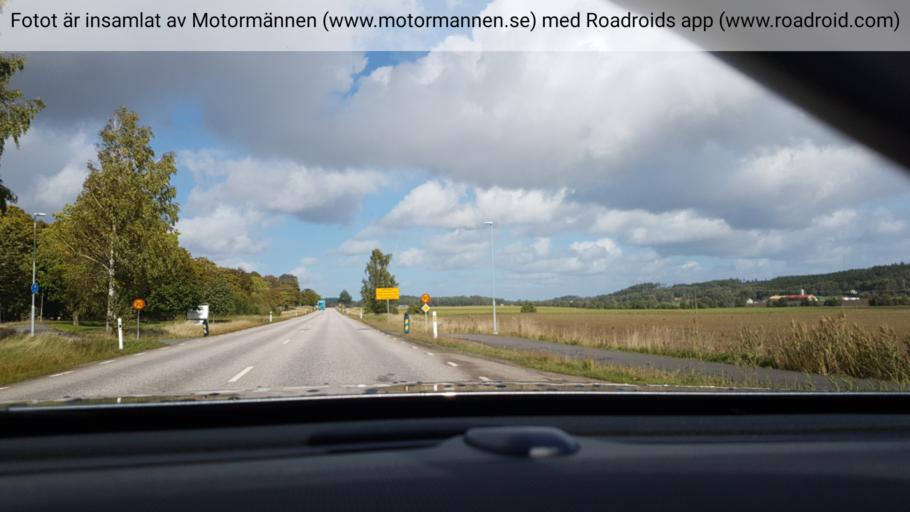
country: SE
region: Vaestra Goetaland
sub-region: Alingsas Kommun
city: Sollebrunn
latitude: 58.0877
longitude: 12.4946
